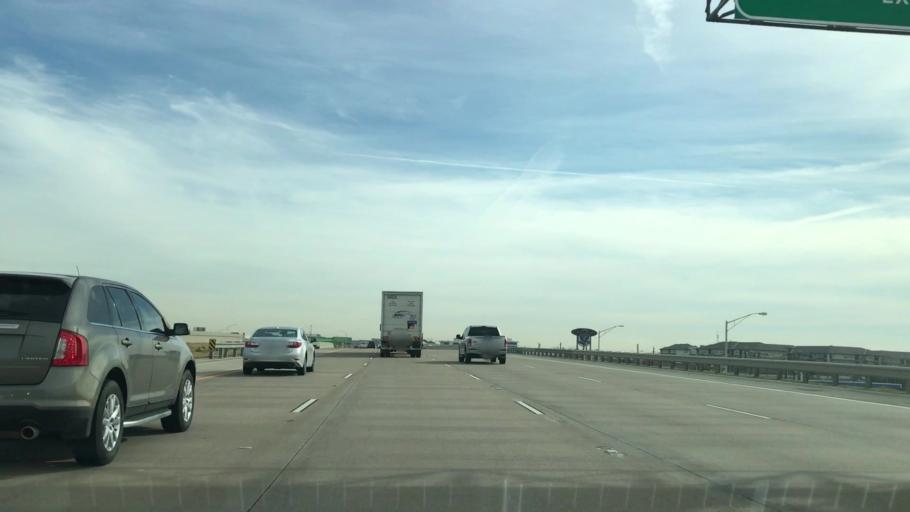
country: US
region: Texas
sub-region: Dallas County
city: Richardson
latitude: 32.9996
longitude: -96.7693
